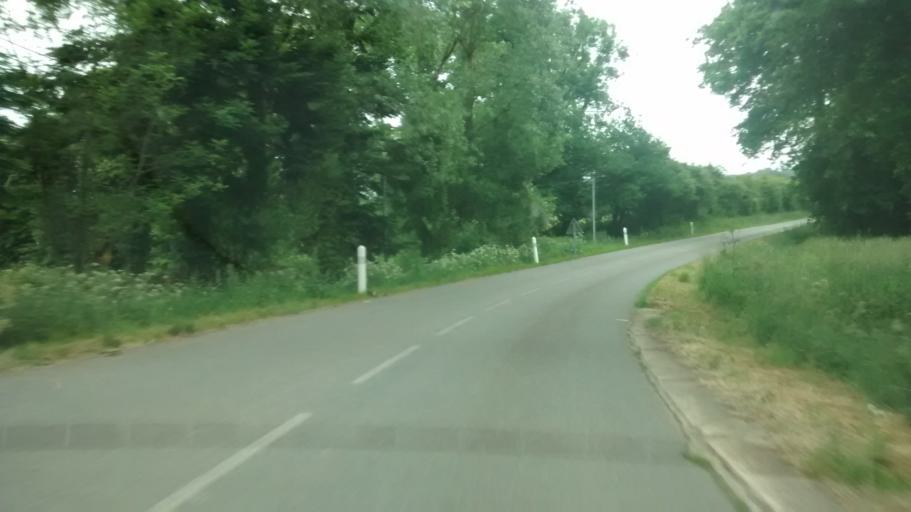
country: FR
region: Brittany
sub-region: Departement du Morbihan
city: Campeneac
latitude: 47.9767
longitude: -2.2764
